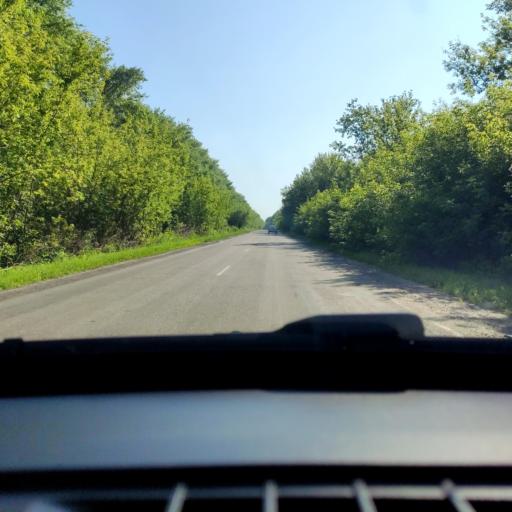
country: RU
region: Voronezj
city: Panino
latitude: 51.6220
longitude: 40.0280
